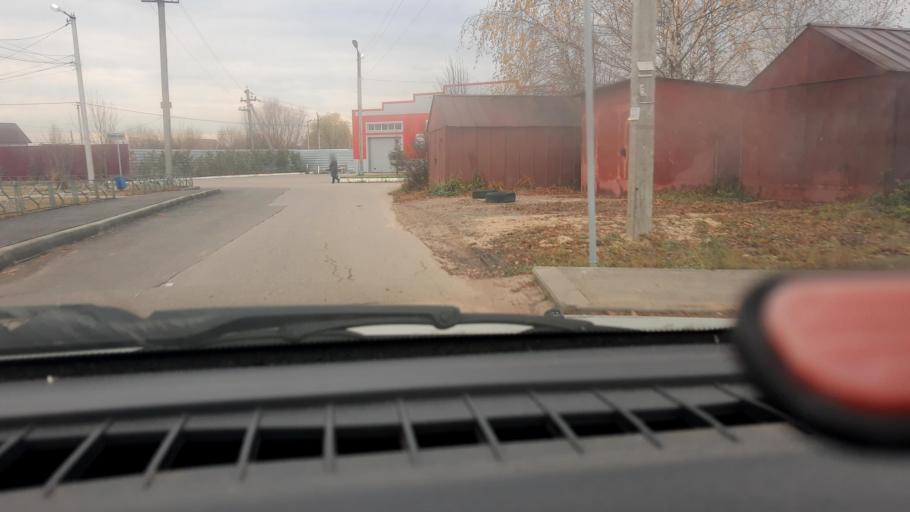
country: RU
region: Nizjnij Novgorod
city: Afonino
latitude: 56.2075
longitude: 44.0973
